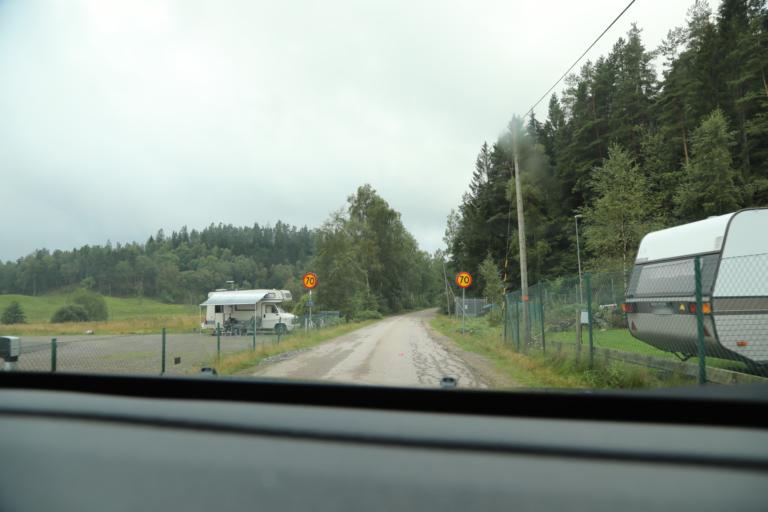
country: SE
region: Halland
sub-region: Falkenbergs Kommun
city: Falkenberg
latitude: 57.1245
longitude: 12.7061
